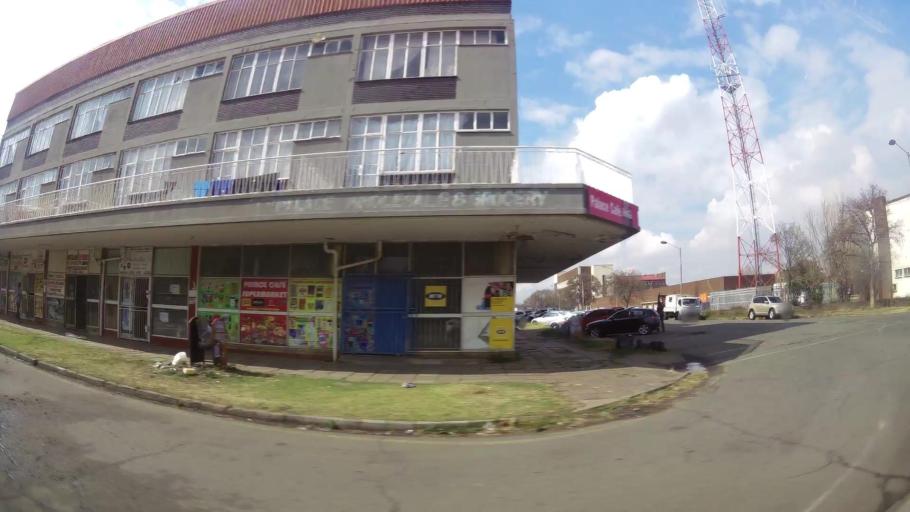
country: ZA
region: Gauteng
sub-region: Sedibeng District Municipality
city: Vereeniging
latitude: -26.6786
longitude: 27.9285
